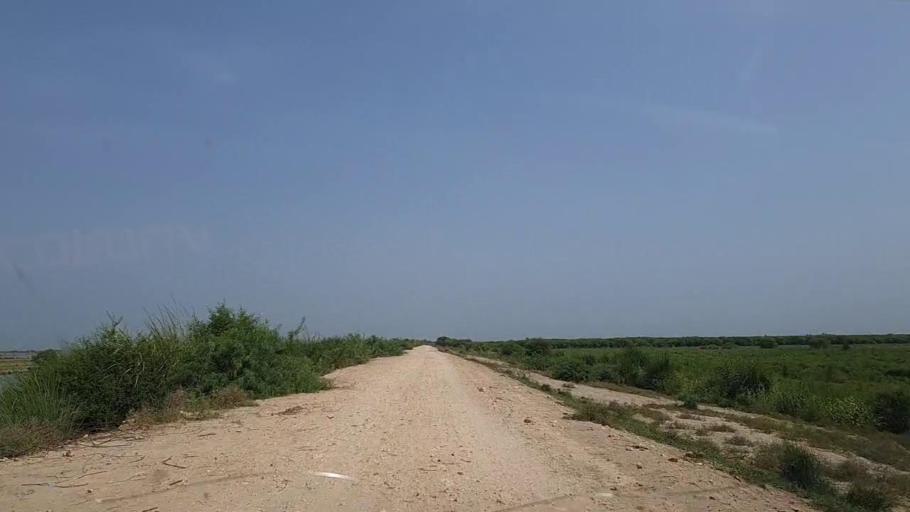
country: PK
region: Sindh
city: Ghotki
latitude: 28.1033
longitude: 69.3988
